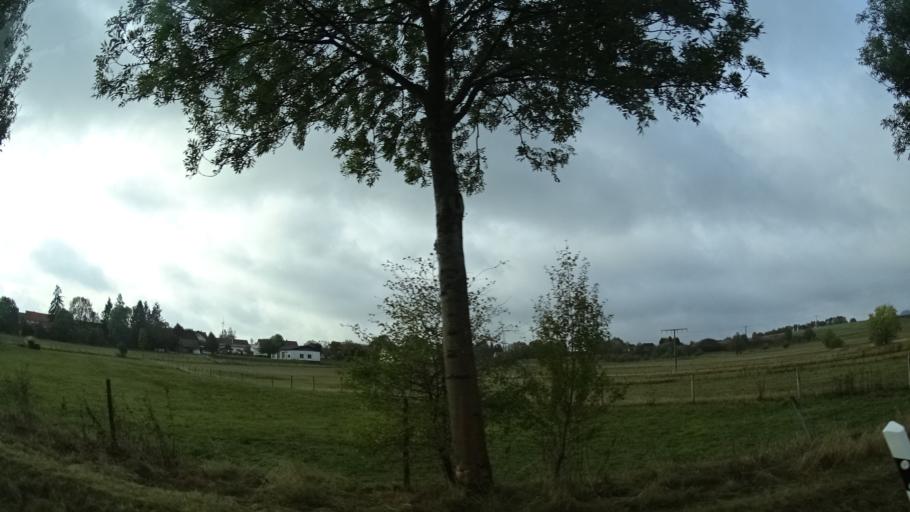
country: DE
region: Hesse
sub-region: Regierungsbezirk Giessen
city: Grebenhain
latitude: 50.4864
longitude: 9.3433
